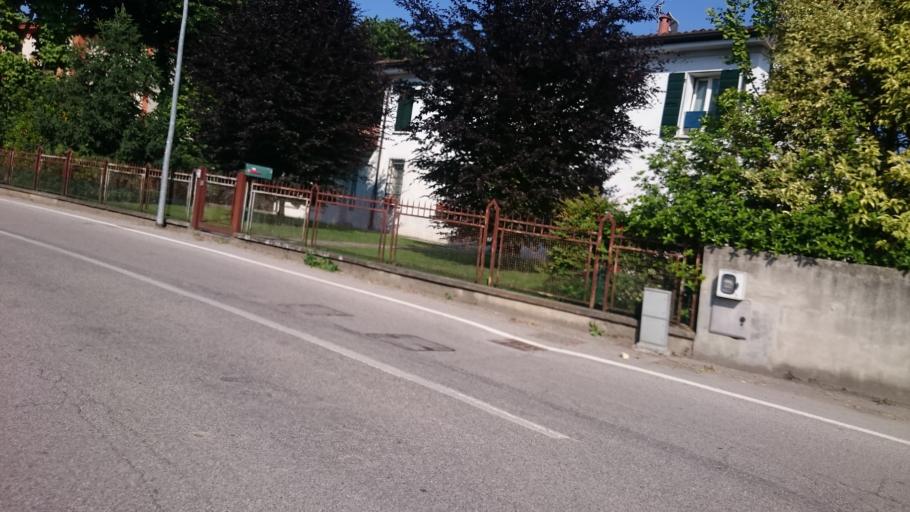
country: IT
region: Lombardy
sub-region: Provincia di Mantova
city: Roncoferraro
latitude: 45.1383
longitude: 10.9407
